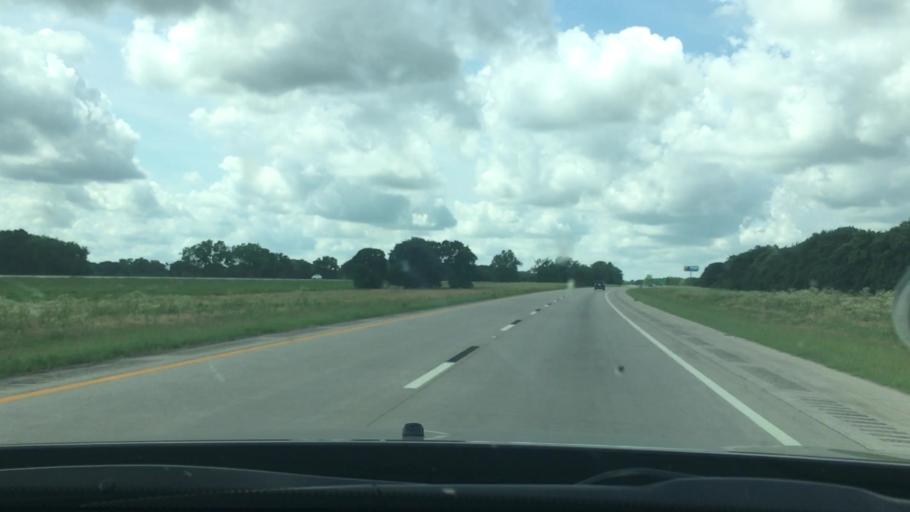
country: US
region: Oklahoma
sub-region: Love County
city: Marietta
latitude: 33.8210
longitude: -97.1311
